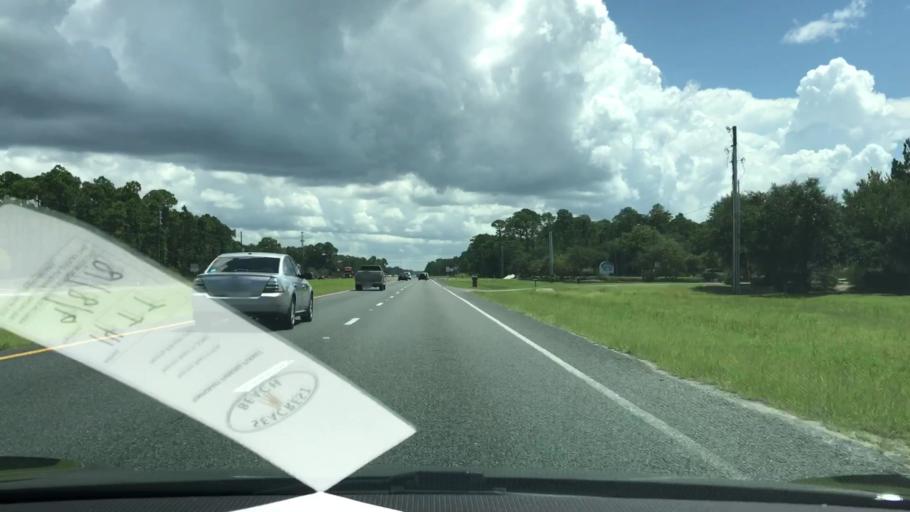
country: US
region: Florida
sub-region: Walton County
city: Miramar Beach
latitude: 30.3739
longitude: -86.2587
